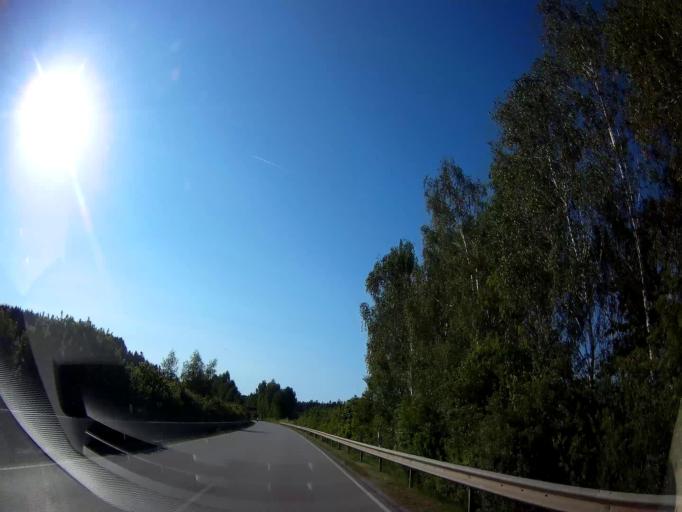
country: DE
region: Bavaria
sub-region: Lower Bavaria
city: Falkenberg
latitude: 48.4488
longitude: 12.7357
